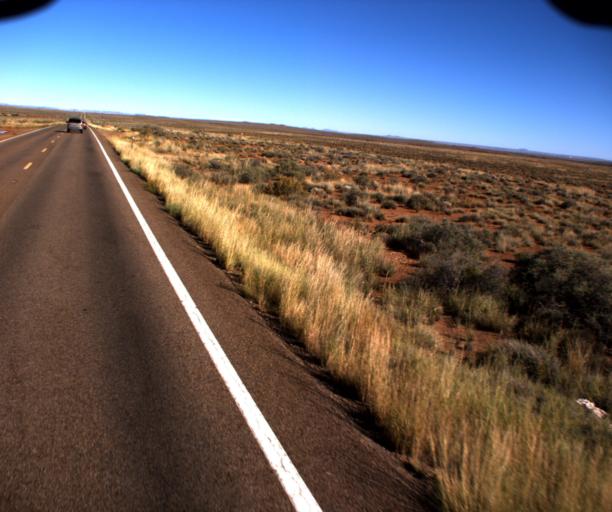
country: US
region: Arizona
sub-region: Navajo County
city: Holbrook
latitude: 34.7603
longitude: -110.1246
